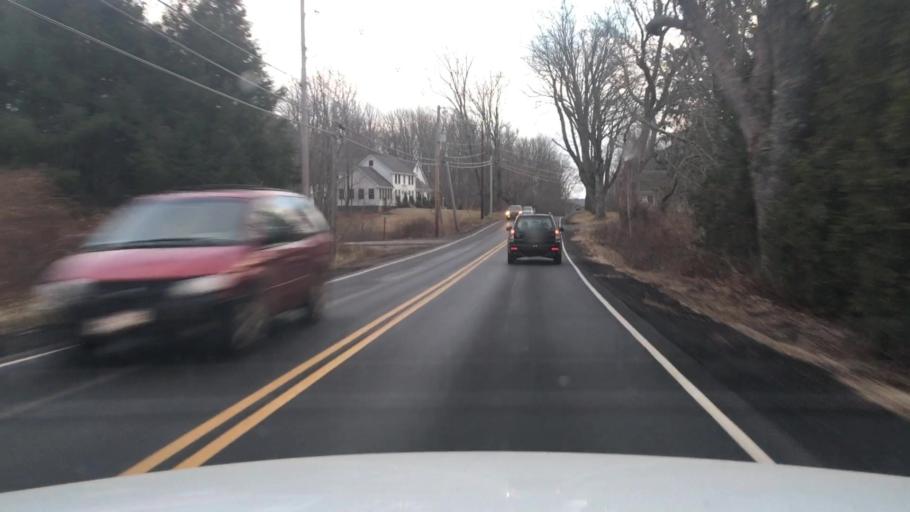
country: US
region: Maine
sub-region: Lincoln County
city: Damariscotta
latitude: 44.0072
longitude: -69.5306
